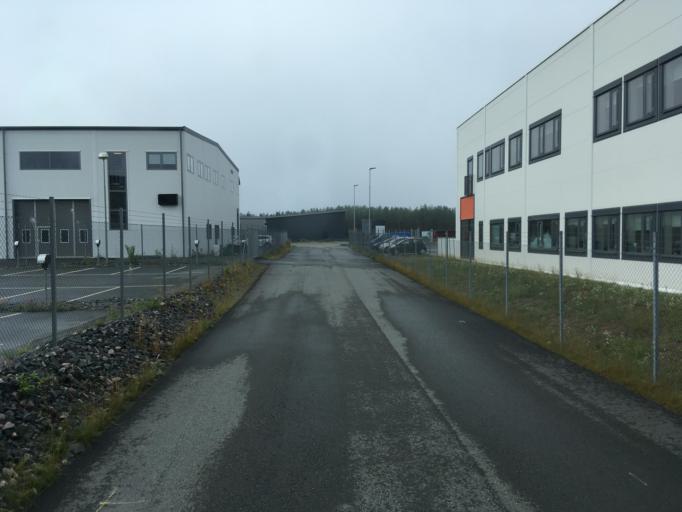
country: SE
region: Joenkoeping
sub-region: Jonkopings Kommun
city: Jonkoping
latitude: 57.7691
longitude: 14.0827
